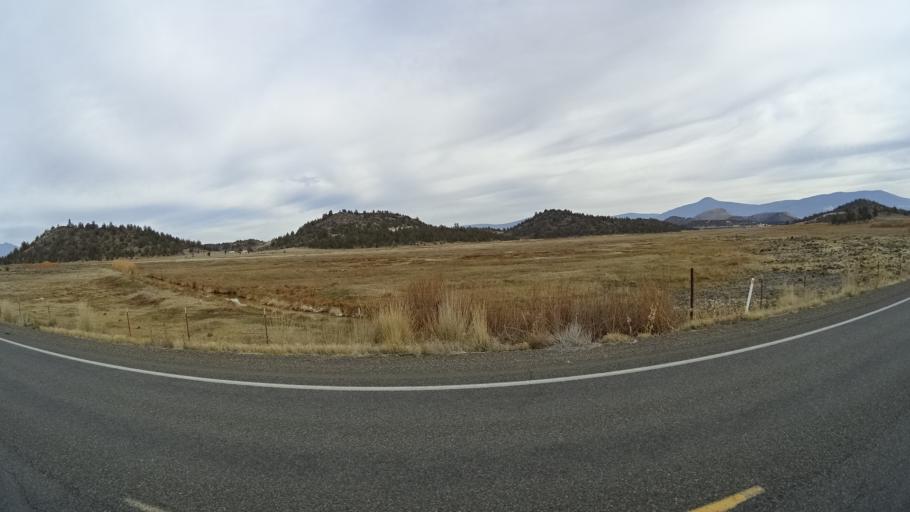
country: US
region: California
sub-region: Siskiyou County
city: Montague
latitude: 41.6466
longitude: -122.4937
